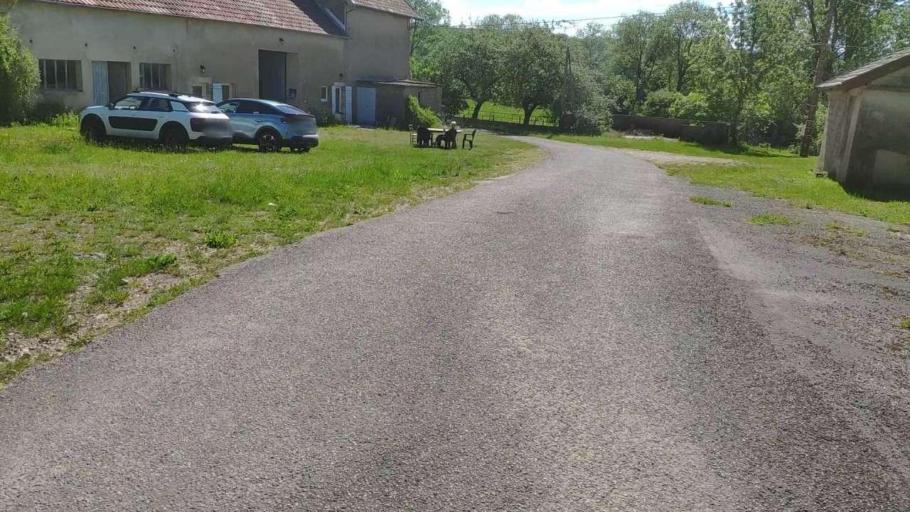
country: FR
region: Franche-Comte
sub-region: Departement du Jura
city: Clairvaux-les-Lacs
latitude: 46.7089
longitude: 5.7664
